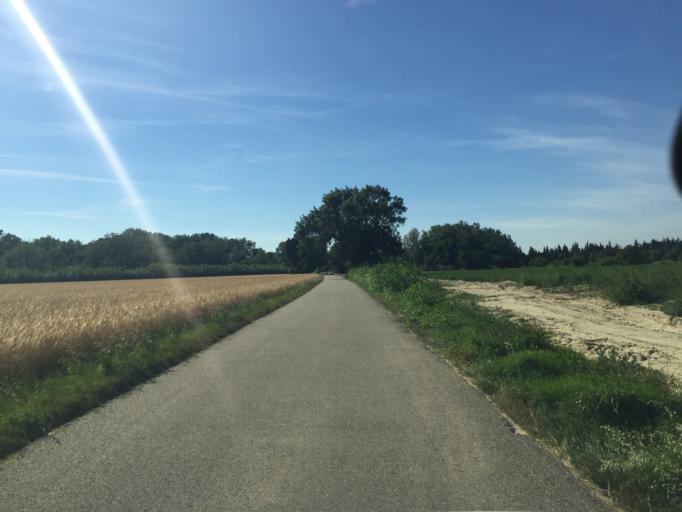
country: FR
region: Provence-Alpes-Cote d'Azur
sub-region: Departement du Vaucluse
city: Caderousse
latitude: 44.0938
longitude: 4.7650
